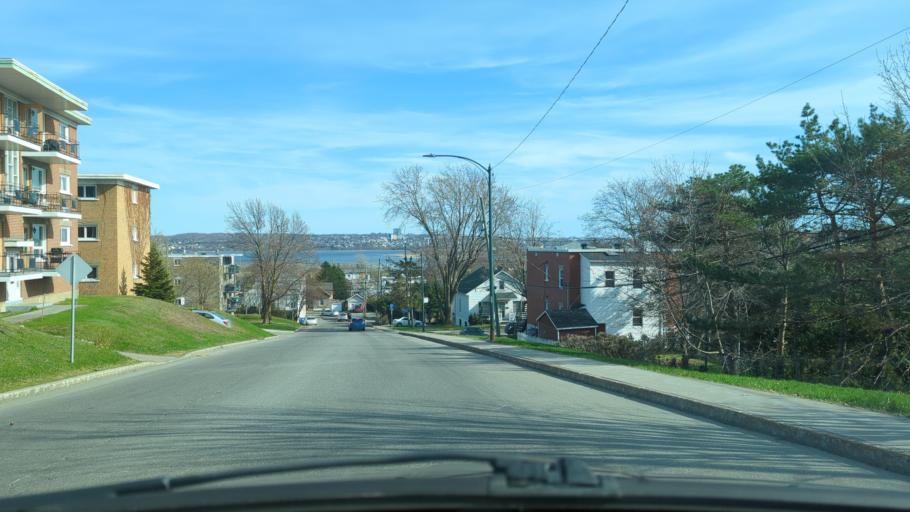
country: CA
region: Quebec
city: Quebec
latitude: 46.8550
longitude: -71.2060
